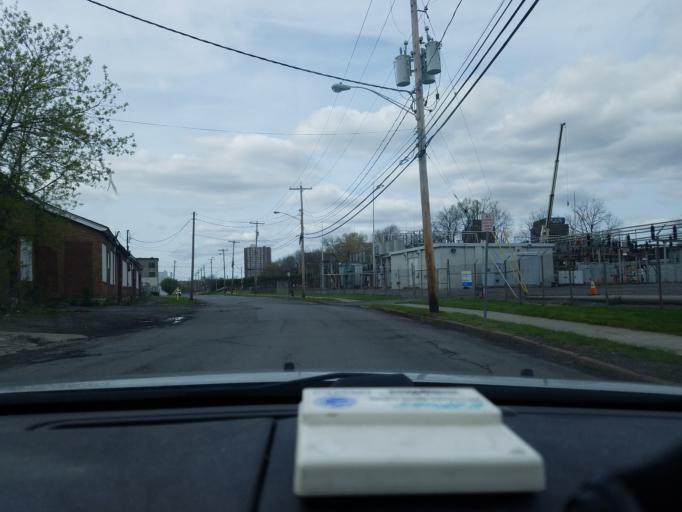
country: US
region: New York
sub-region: Onondaga County
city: Syracuse
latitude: 43.0392
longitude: -76.1526
